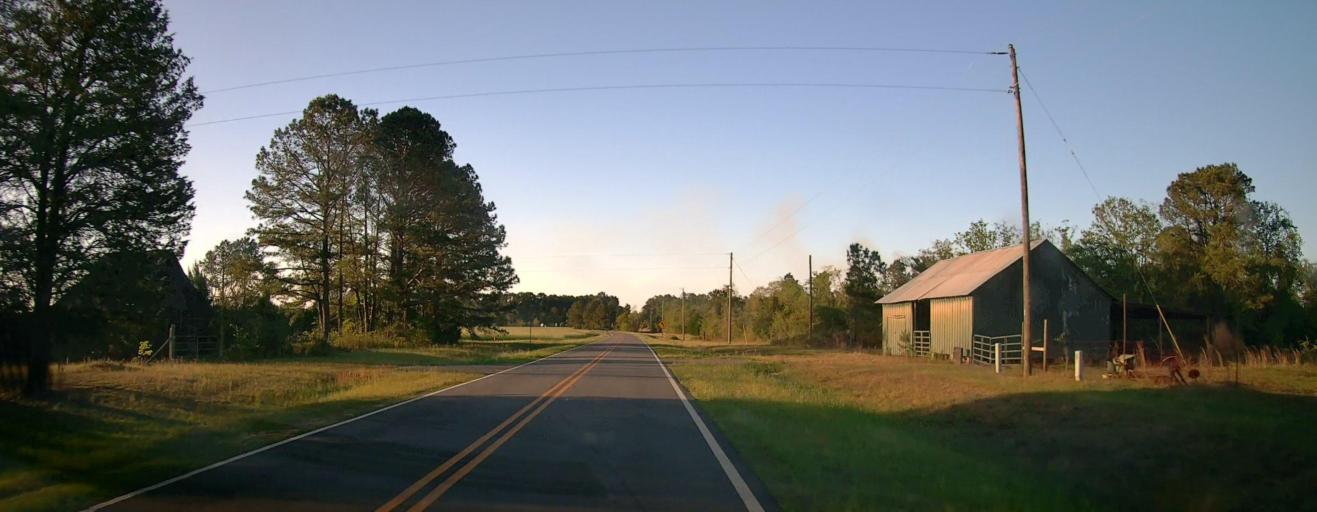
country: US
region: Georgia
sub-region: Marion County
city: Buena Vista
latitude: 32.4561
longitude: -84.4252
